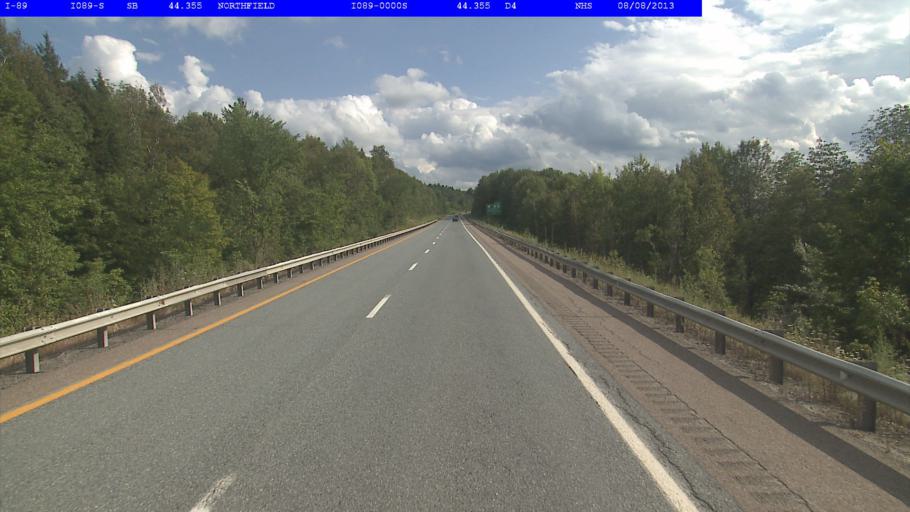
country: US
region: Vermont
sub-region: Washington County
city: Northfield
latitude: 44.1349
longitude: -72.6014
